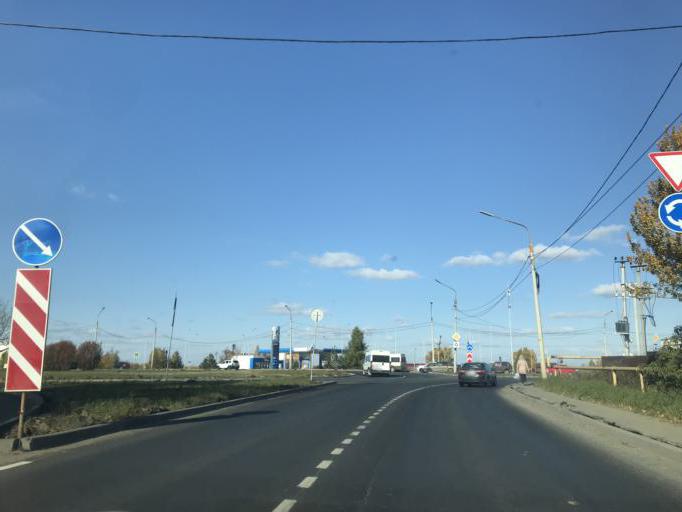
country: RU
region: Chelyabinsk
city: Roshchino
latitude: 55.2399
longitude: 61.3187
